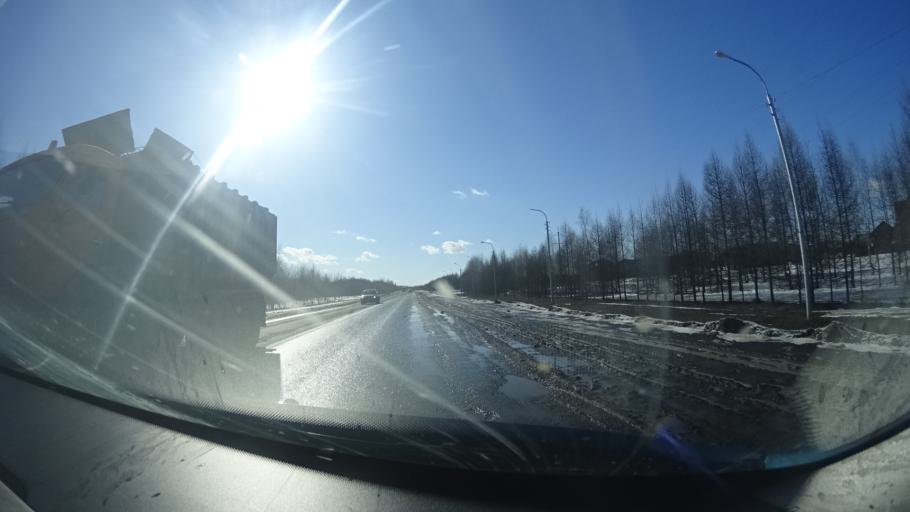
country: RU
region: Bashkortostan
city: Chishmy
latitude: 54.5808
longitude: 55.3728
